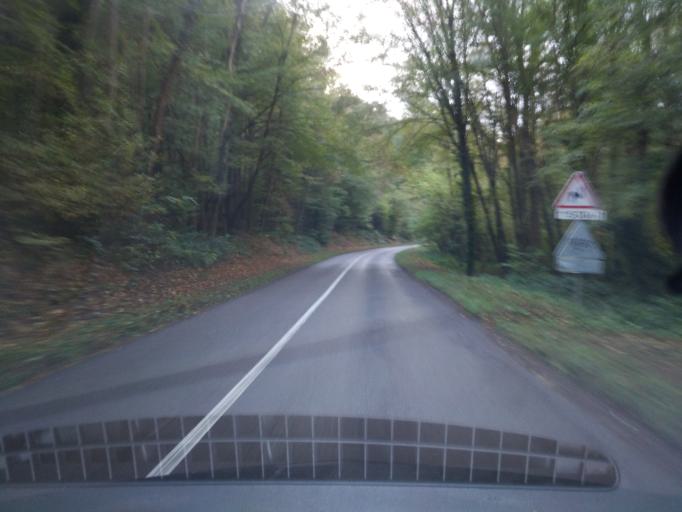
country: FR
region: Ile-de-France
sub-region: Departement de l'Essonne
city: Les Molieres
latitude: 48.6882
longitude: 2.0649
